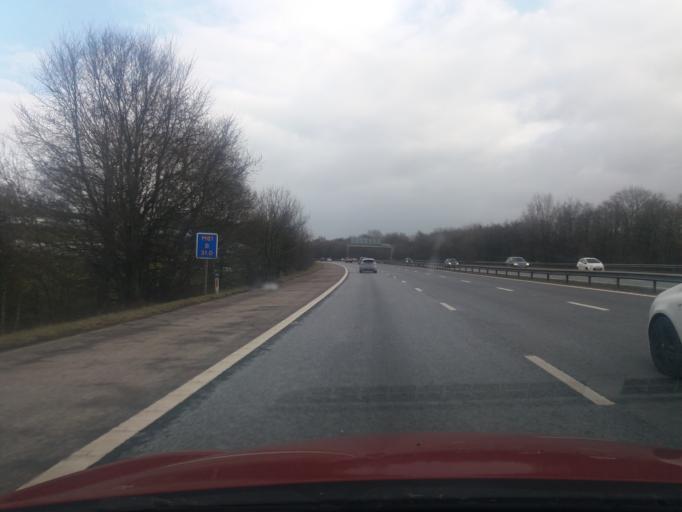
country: GB
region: England
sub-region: Lancashire
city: Clayton-le-Woods
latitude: 53.6998
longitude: -2.6315
